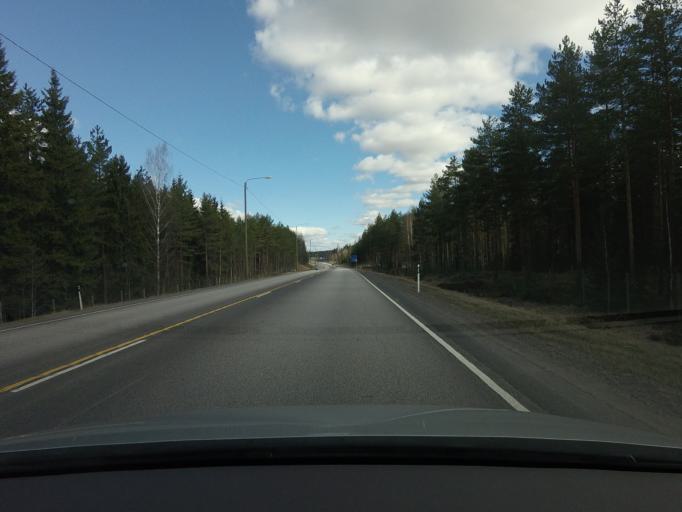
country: FI
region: Uusimaa
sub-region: Loviisa
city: Perna
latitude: 60.5097
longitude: 25.9658
